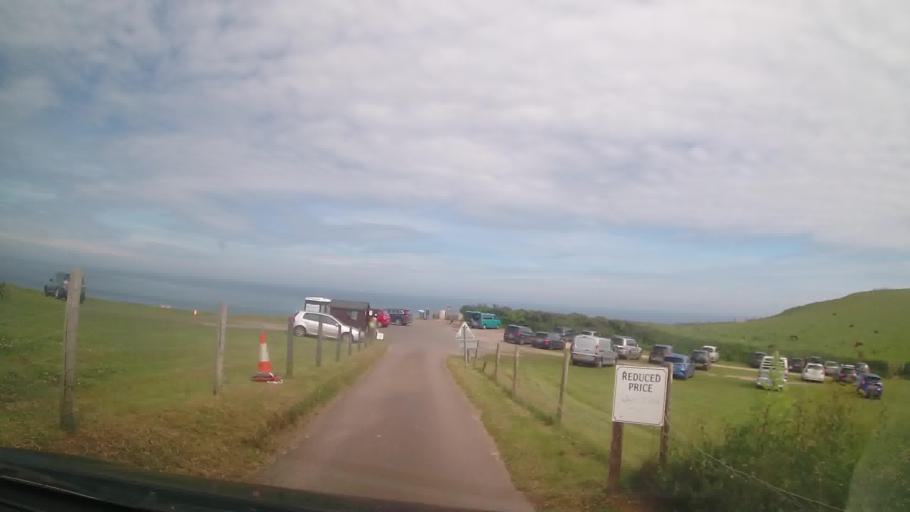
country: GB
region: England
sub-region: Devon
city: Salcombe
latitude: 50.2260
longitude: -3.6555
